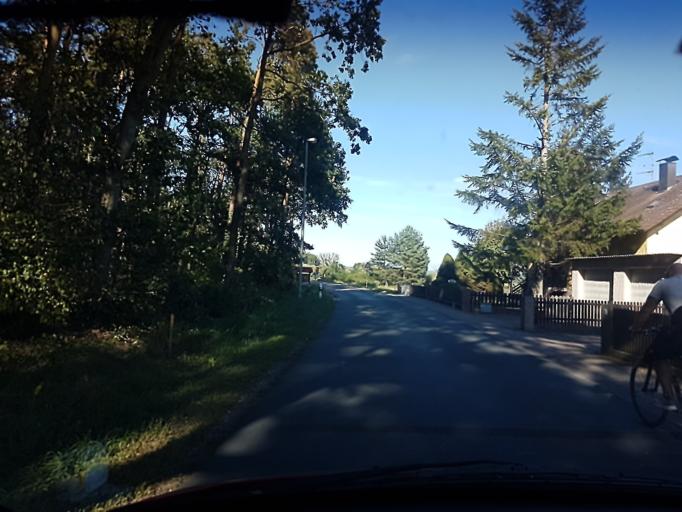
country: DE
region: Bavaria
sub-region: Upper Franconia
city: Hallerndorf
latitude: 49.7352
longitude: 10.9430
